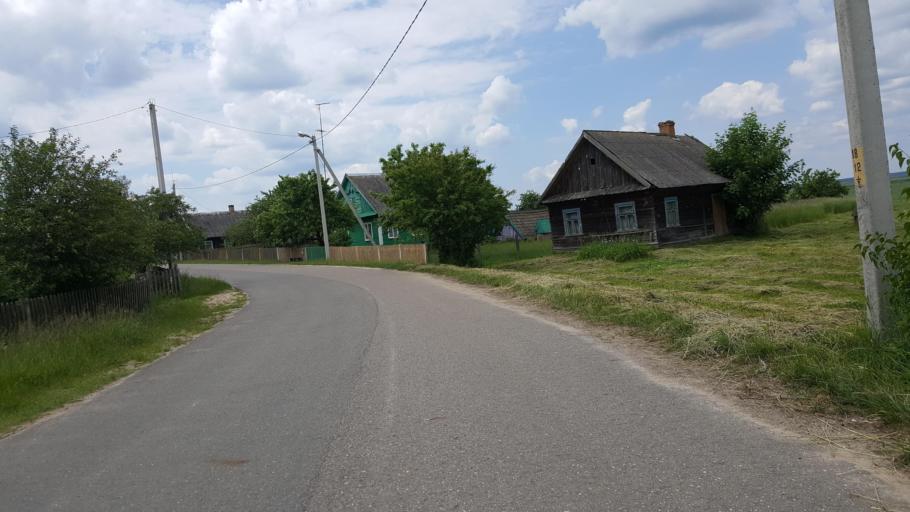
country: PL
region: Podlasie
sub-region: Powiat hajnowski
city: Bialowieza
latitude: 52.6268
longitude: 24.0838
